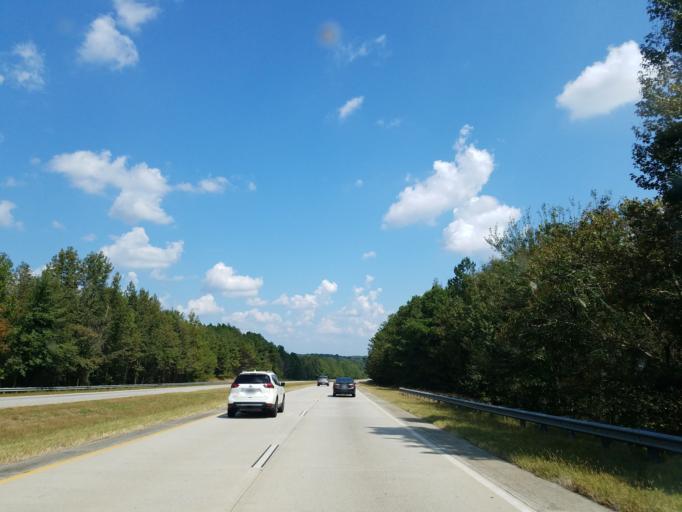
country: US
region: Georgia
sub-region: Barrow County
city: Statham
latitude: 33.9597
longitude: -83.6456
